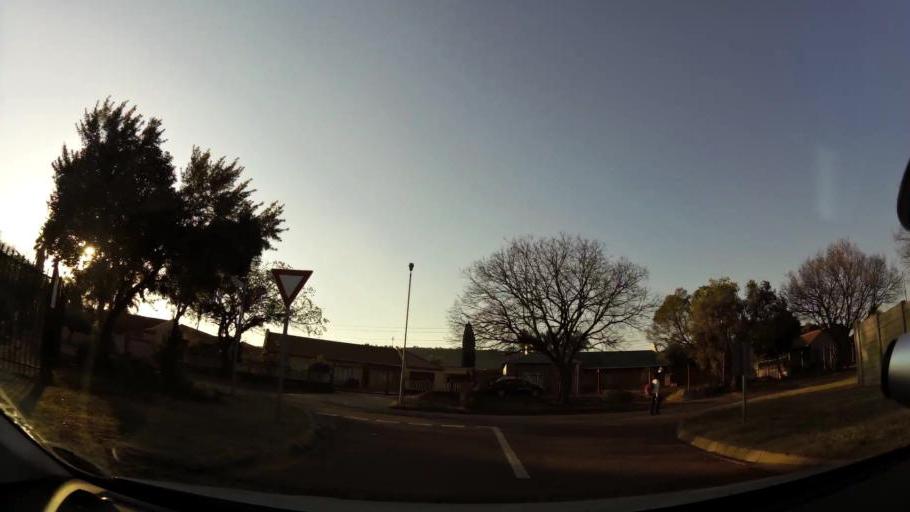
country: ZA
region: Gauteng
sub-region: City of Tshwane Metropolitan Municipality
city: Pretoria
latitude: -25.7377
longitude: 28.1102
